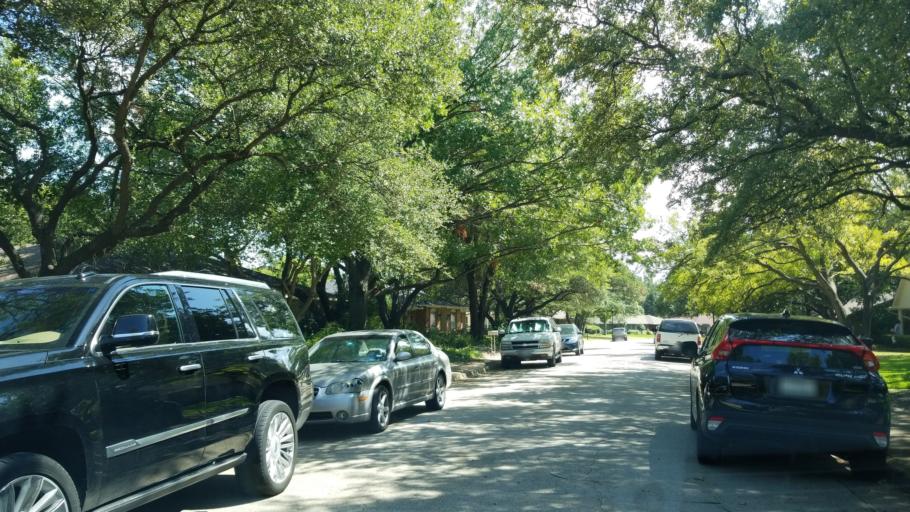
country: US
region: Texas
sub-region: Dallas County
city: Addison
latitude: 32.9536
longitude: -96.7853
